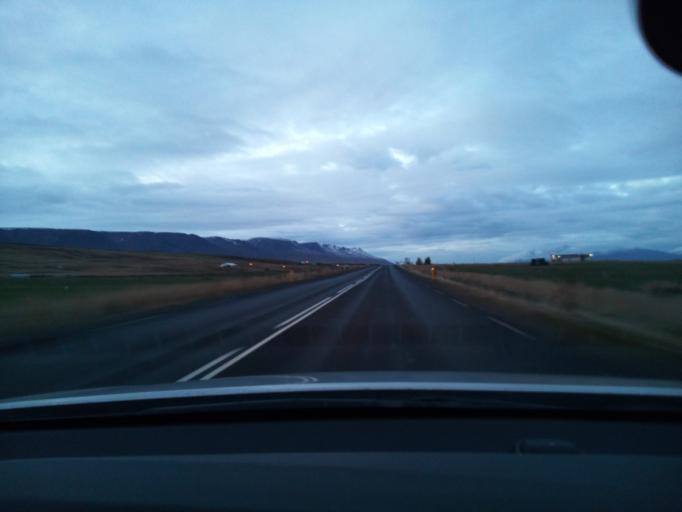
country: IS
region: Northeast
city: Akureyri
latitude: 65.7264
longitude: -18.1833
